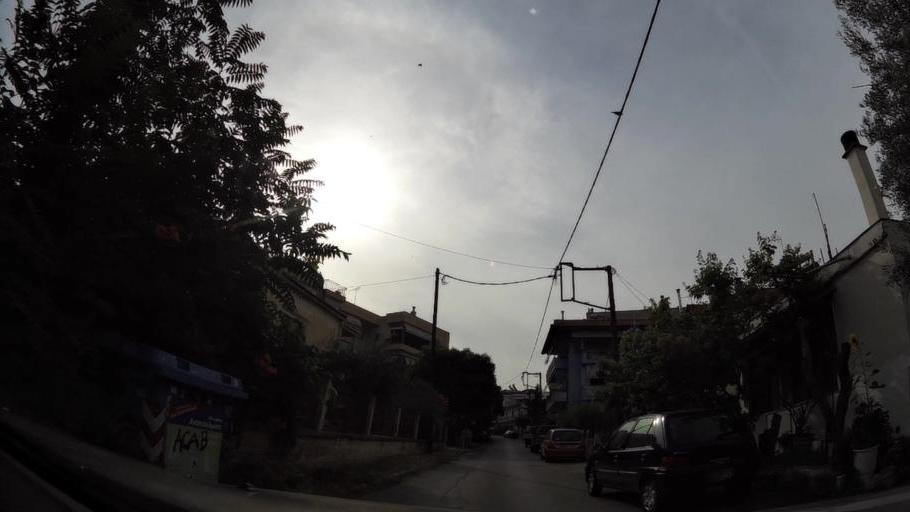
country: GR
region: Central Macedonia
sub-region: Nomos Thessalonikis
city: Thermi
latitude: 40.5458
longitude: 23.0151
